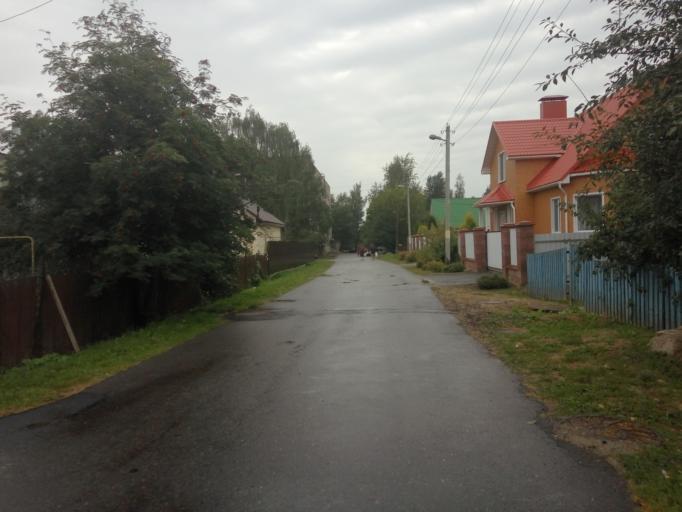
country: BY
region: Vitebsk
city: Vitebsk
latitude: 55.2020
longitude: 30.2525
